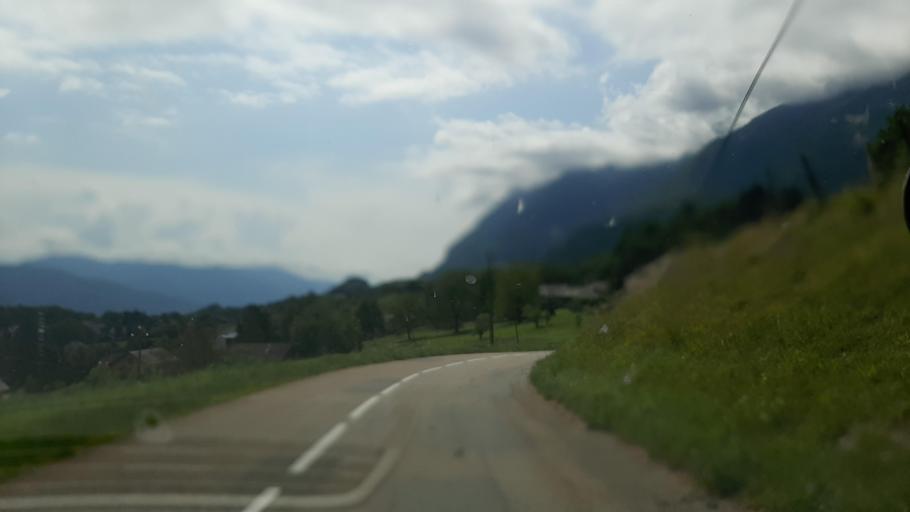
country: FR
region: Rhone-Alpes
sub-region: Departement de la Savoie
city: Frontenex
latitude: 45.6615
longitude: 6.3087
